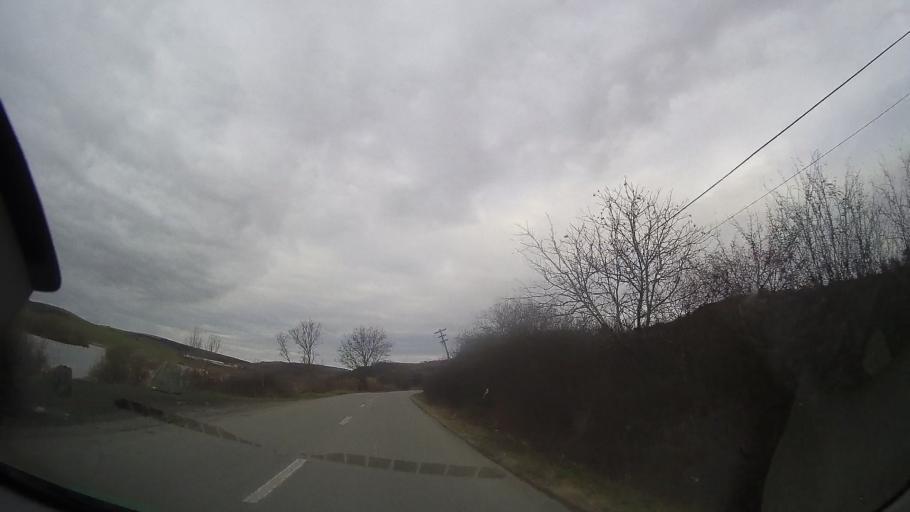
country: RO
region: Mures
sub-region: Comuna Faragau
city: Faragau
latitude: 46.7493
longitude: 24.5280
